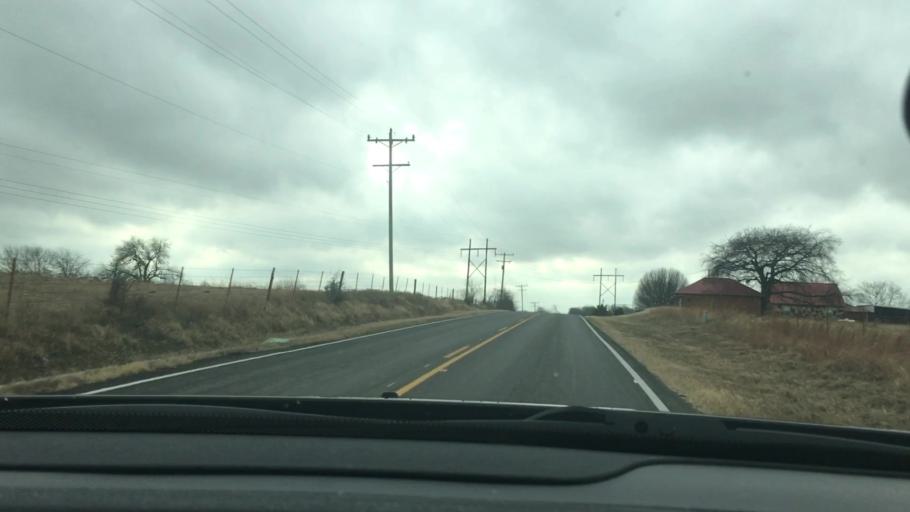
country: US
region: Oklahoma
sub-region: Bryan County
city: Durant
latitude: 34.1372
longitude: -96.4949
